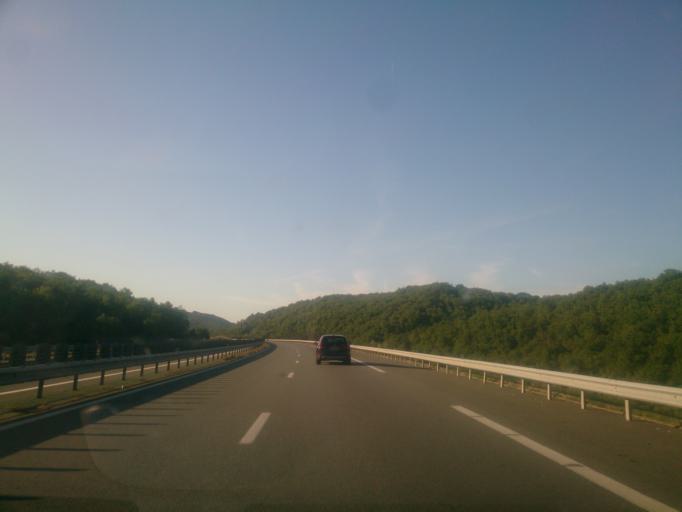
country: FR
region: Midi-Pyrenees
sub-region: Departement du Lot
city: Souillac
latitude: 44.8358
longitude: 1.4957
